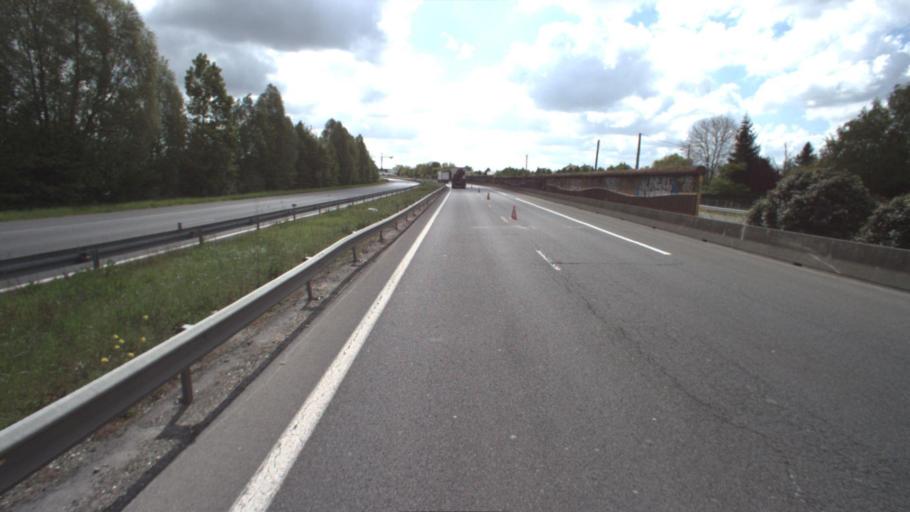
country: FR
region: Ile-de-France
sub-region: Departement de Seine-et-Marne
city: Fontenay-Tresigny
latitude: 48.7064
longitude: 2.8812
